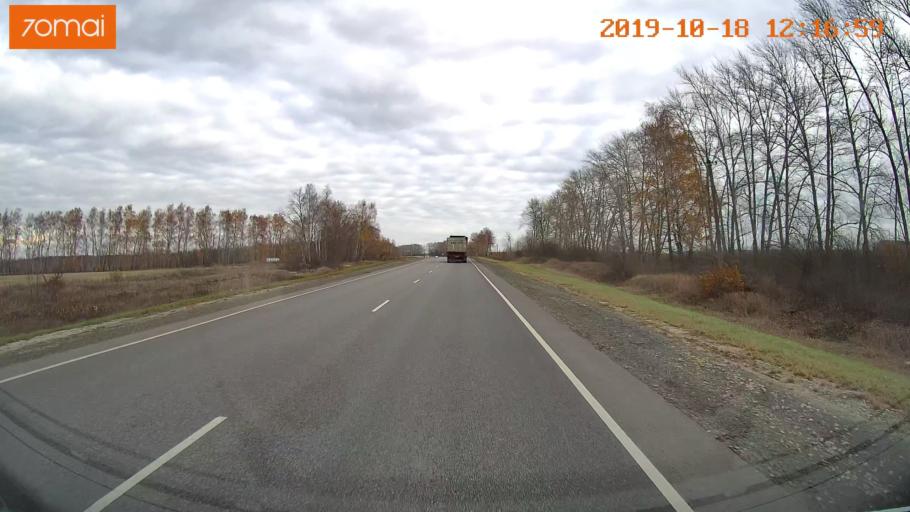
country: RU
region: Rjazan
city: Zakharovo
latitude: 54.4549
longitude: 39.4351
